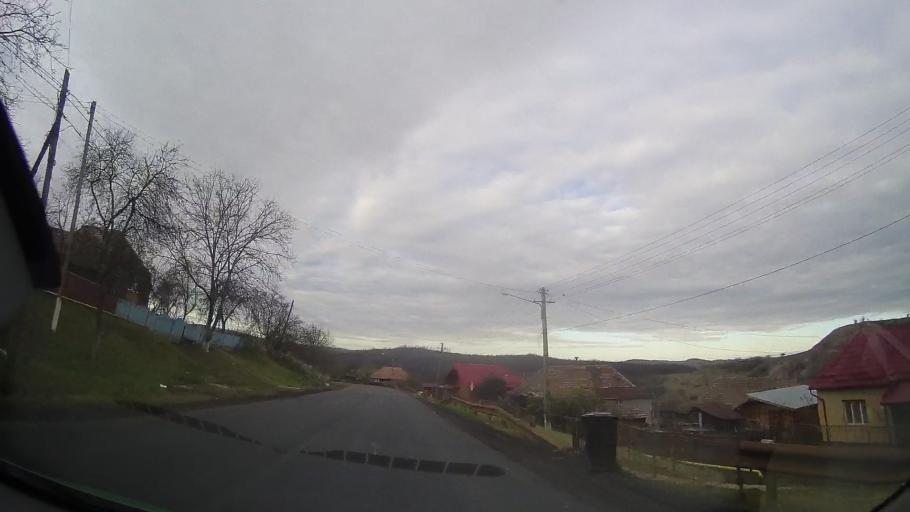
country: RO
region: Bistrita-Nasaud
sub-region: Comuna Silvasu de Campie
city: Silvasu de Campie
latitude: 46.7784
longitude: 24.3056
